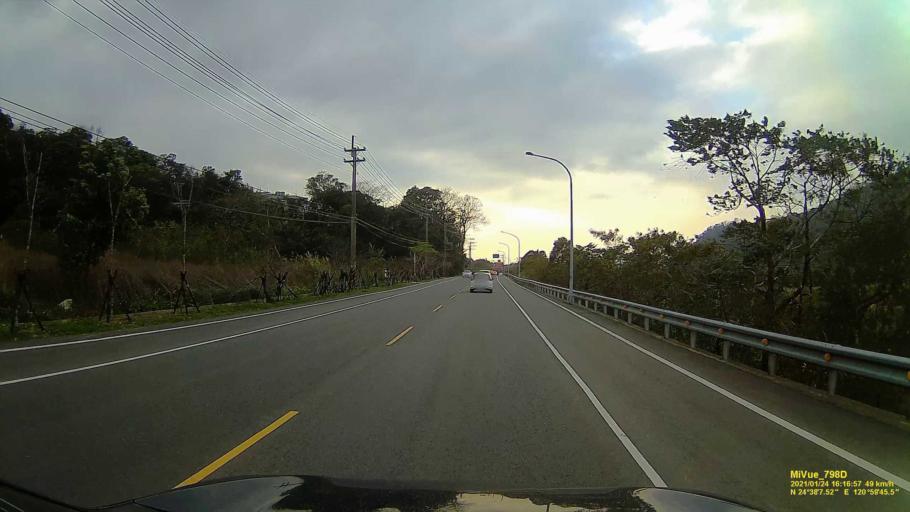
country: TW
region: Taiwan
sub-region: Hsinchu
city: Hsinchu
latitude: 24.6354
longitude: 120.9957
